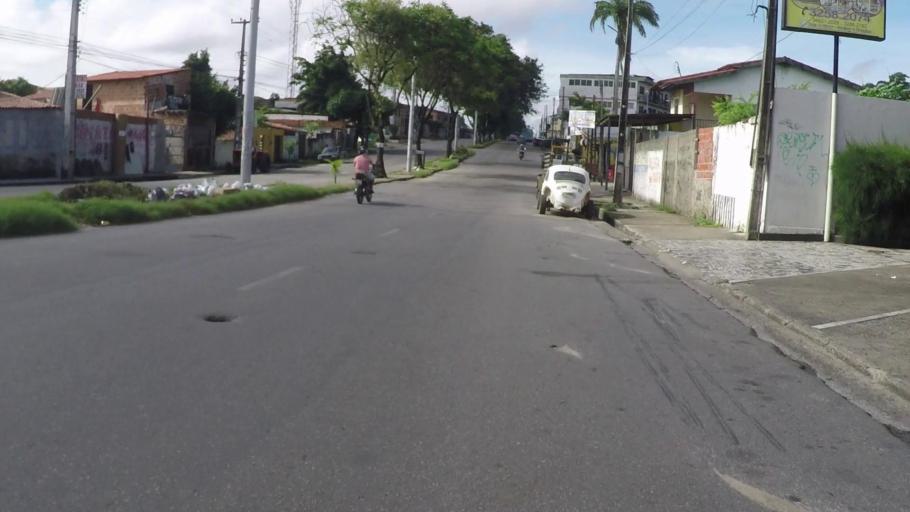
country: BR
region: Ceara
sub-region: Fortaleza
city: Fortaleza
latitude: -3.7153
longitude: -38.5886
